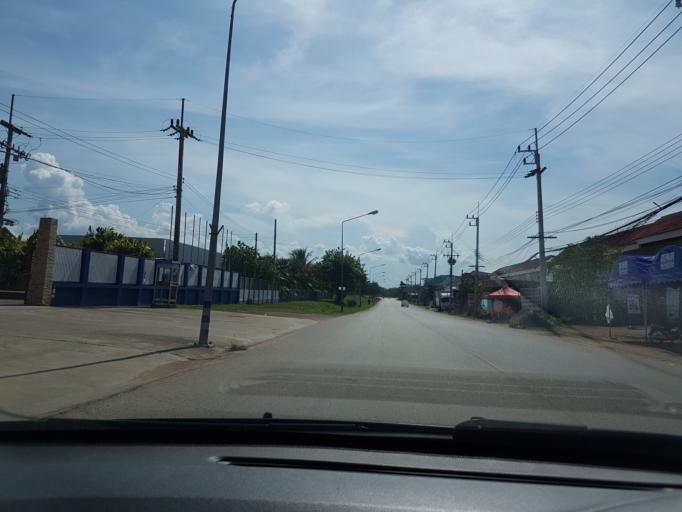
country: TH
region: Lampang
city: Ko Kha
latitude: 18.2121
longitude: 99.3898
